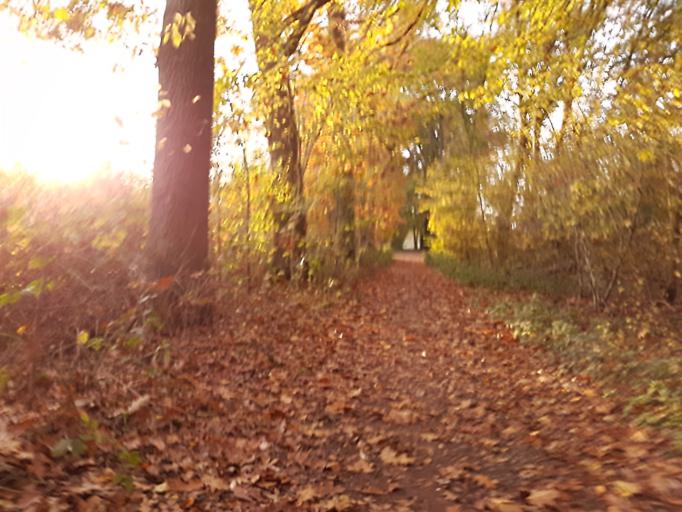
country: BE
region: Flanders
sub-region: Provincie Antwerpen
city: Ranst
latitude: 51.2025
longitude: 4.5639
